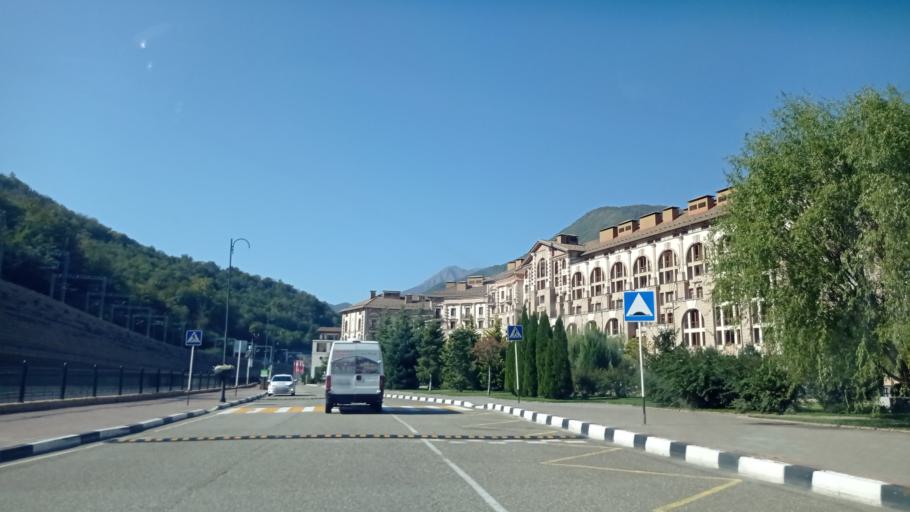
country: RU
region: Krasnodarskiy
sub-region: Sochi City
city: Krasnaya Polyana
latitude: 43.6824
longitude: 40.2605
